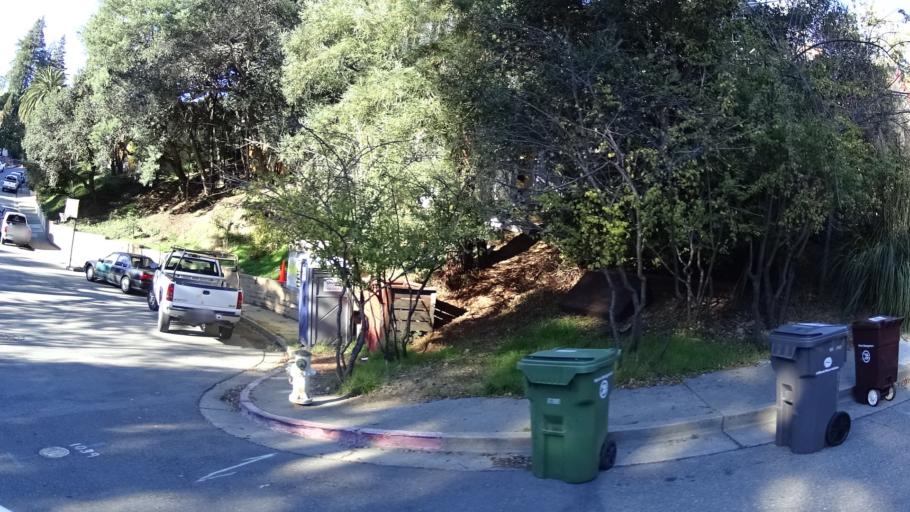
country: US
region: California
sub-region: Alameda County
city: Piedmont
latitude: 37.8255
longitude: -122.2206
